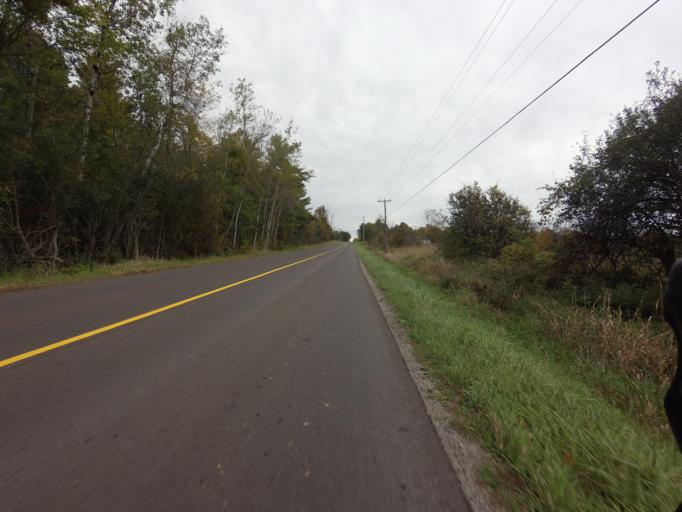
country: CA
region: Ontario
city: Gananoque
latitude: 44.5824
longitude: -76.0492
